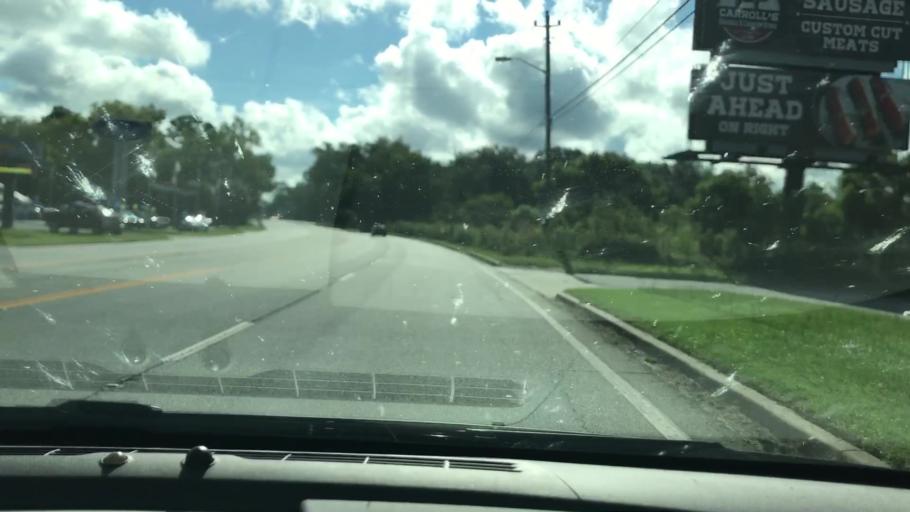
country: US
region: Georgia
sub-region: Worth County
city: Sylvester
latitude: 31.5314
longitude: -83.8512
